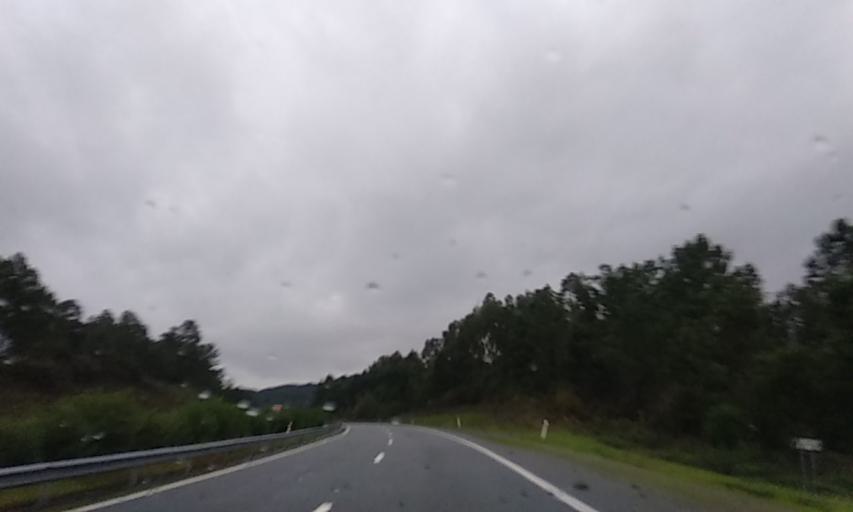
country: PT
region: Braga
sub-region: Barcelos
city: Galegos
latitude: 41.5647
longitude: -8.5364
